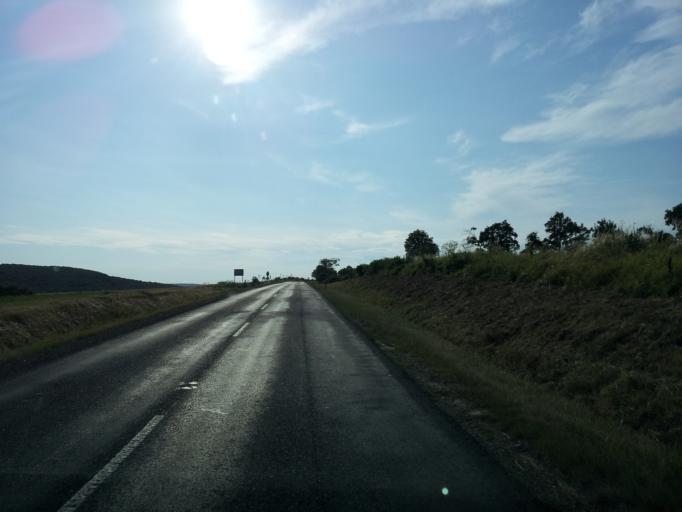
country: HU
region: Veszprem
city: Urkut
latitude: 46.9920
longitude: 17.6670
